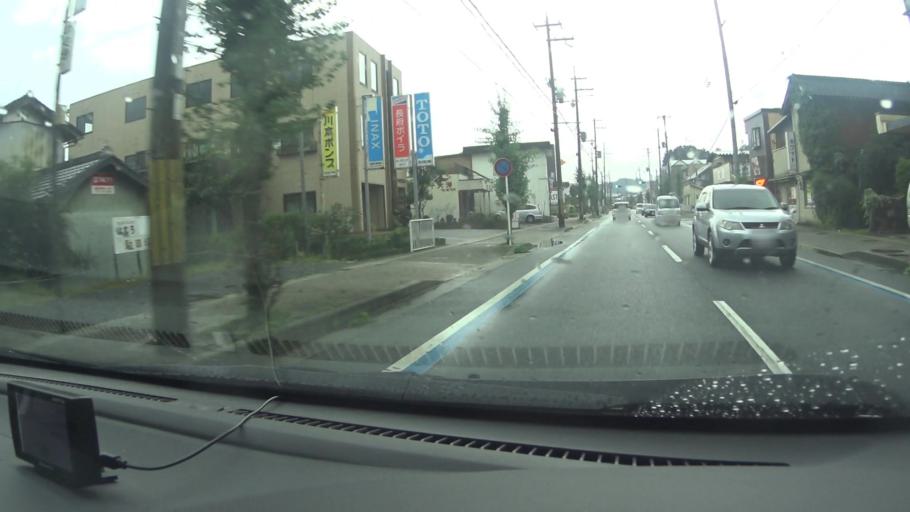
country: JP
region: Kyoto
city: Ayabe
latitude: 35.3027
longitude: 135.2358
